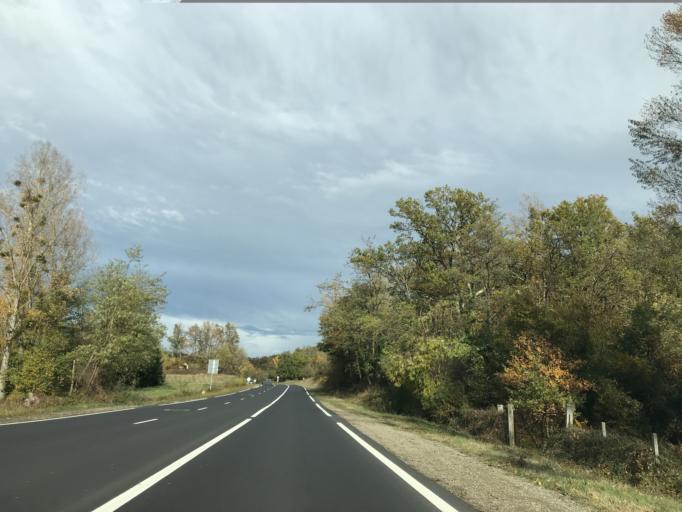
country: FR
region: Auvergne
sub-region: Departement du Puy-de-Dome
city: Peschadoires
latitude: 45.8498
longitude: 3.5075
